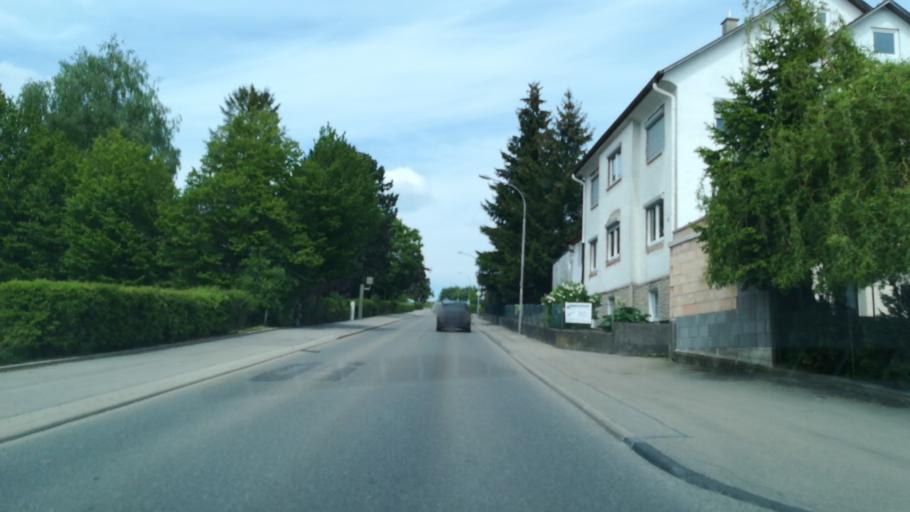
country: DE
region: Baden-Wuerttemberg
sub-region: Freiburg Region
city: Stockach
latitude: 47.8566
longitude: 9.0185
